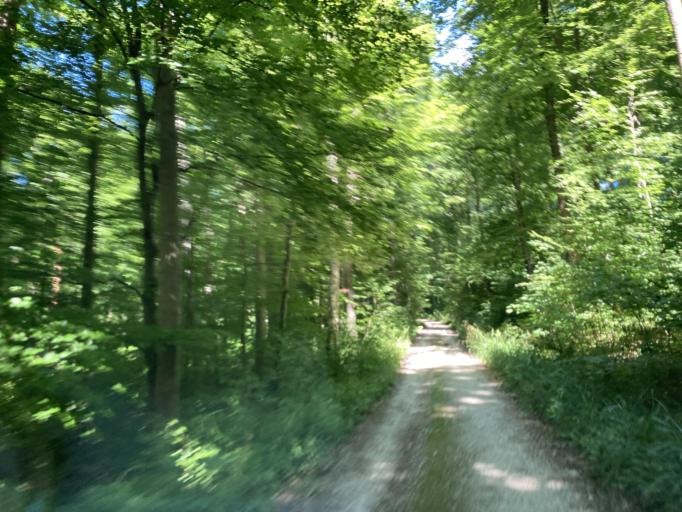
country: DE
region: Baden-Wuerttemberg
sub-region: Tuebingen Region
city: Gomaringen
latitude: 48.4466
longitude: 9.1212
